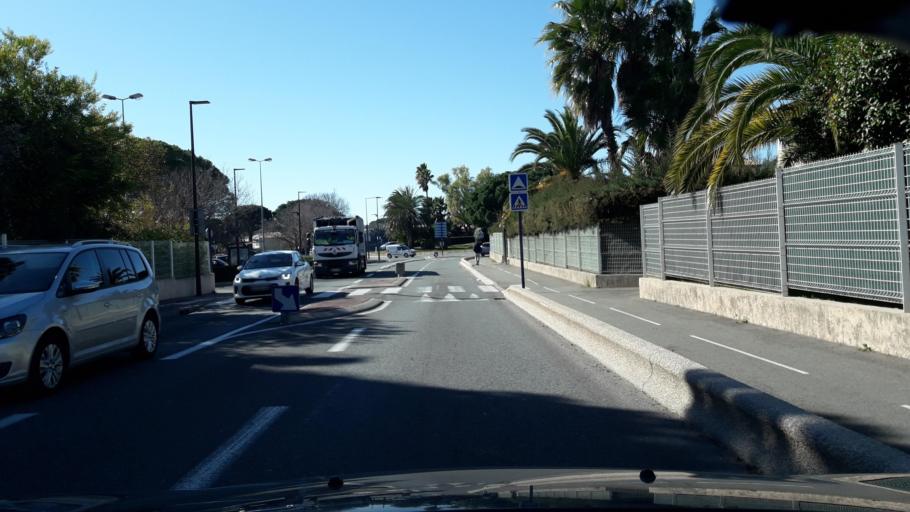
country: FR
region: Provence-Alpes-Cote d'Azur
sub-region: Departement du Var
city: Frejus
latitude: 43.4387
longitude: 6.7559
